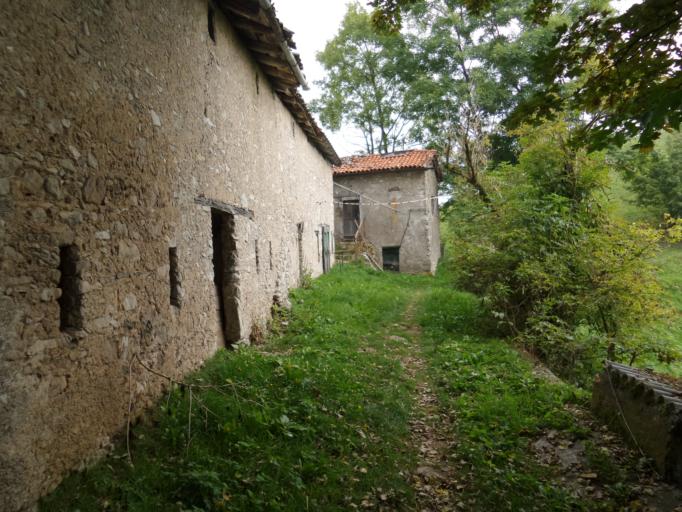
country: IT
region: Lombardy
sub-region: Provincia di Lecco
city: Ballabio
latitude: 45.9062
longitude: 9.4003
